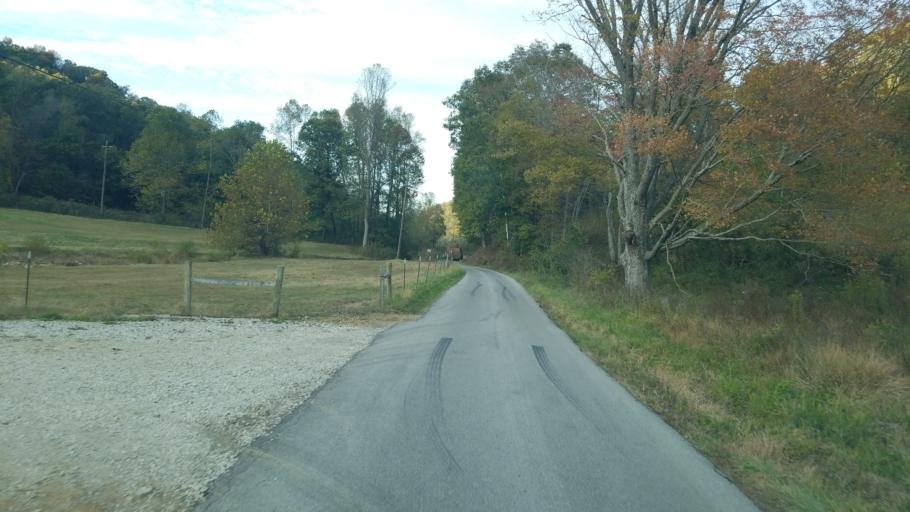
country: US
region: Kentucky
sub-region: Lewis County
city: Vanceburg
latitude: 38.4913
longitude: -83.4874
